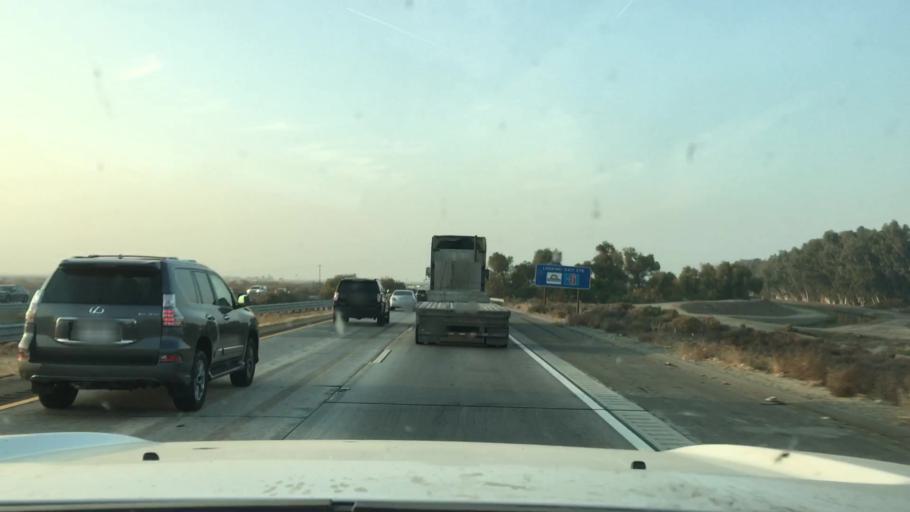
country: US
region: California
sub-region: Kern County
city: Lost Hills
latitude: 35.5995
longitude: -119.6391
